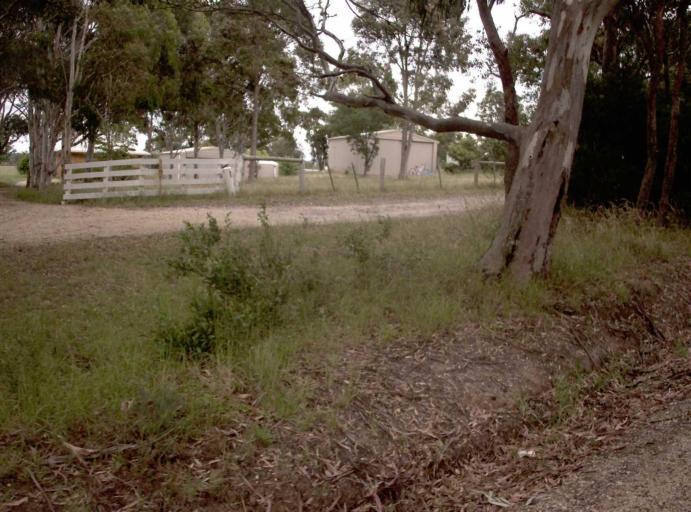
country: AU
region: Victoria
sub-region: East Gippsland
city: Bairnsdale
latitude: -37.7918
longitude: 147.6073
